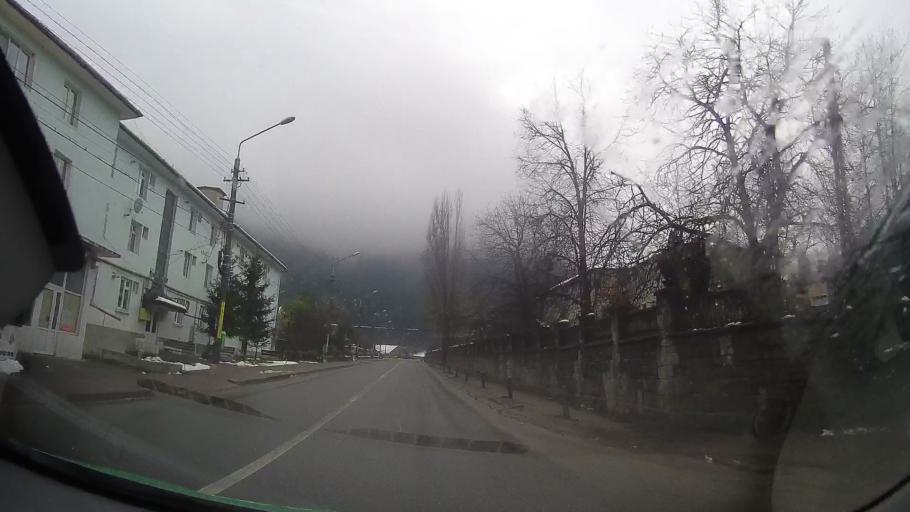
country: RO
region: Neamt
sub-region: Comuna Bicaz
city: Bicaz
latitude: 46.9027
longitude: 26.0740
